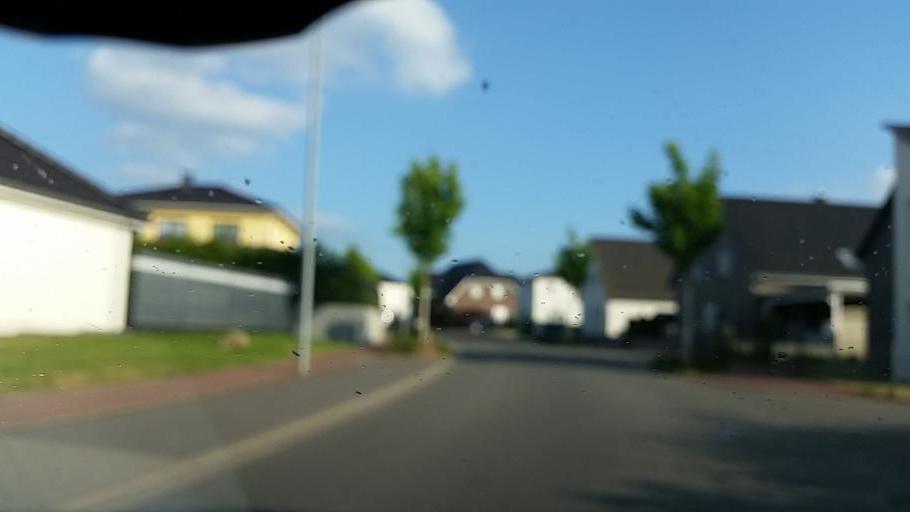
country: DE
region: Lower Saxony
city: Weyhausen
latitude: 52.3988
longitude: 10.7034
